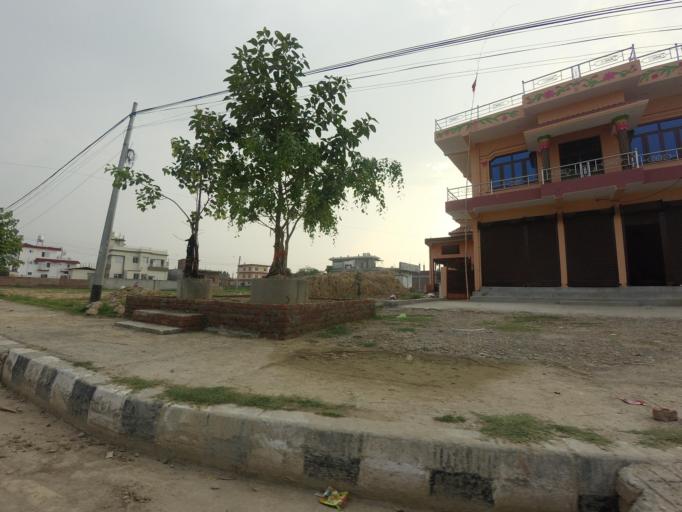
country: NP
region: Western Region
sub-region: Lumbini Zone
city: Bhairahawa
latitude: 27.5013
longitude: 83.4438
